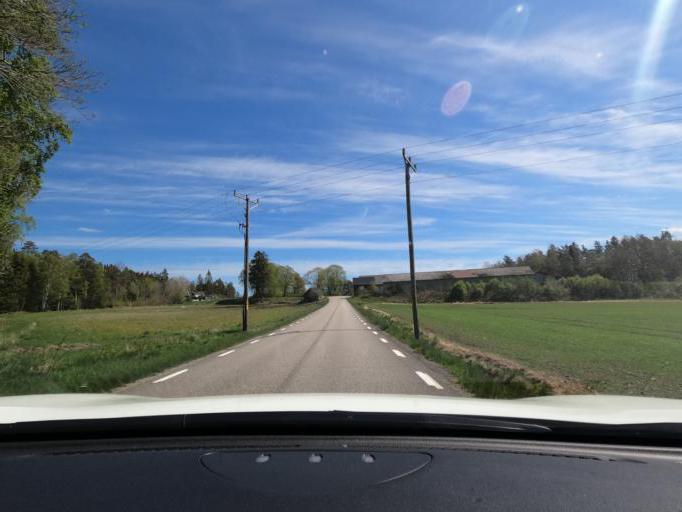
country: SE
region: Vaestra Goetaland
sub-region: Marks Kommun
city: Horred
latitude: 57.4245
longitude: 12.3511
